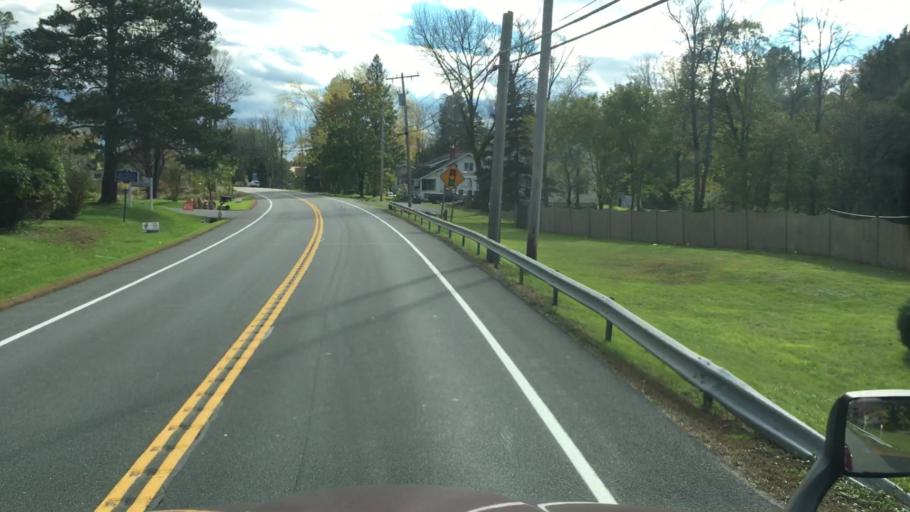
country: US
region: New York
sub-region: Saratoga County
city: Ballston Spa
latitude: 42.9587
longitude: -73.8654
